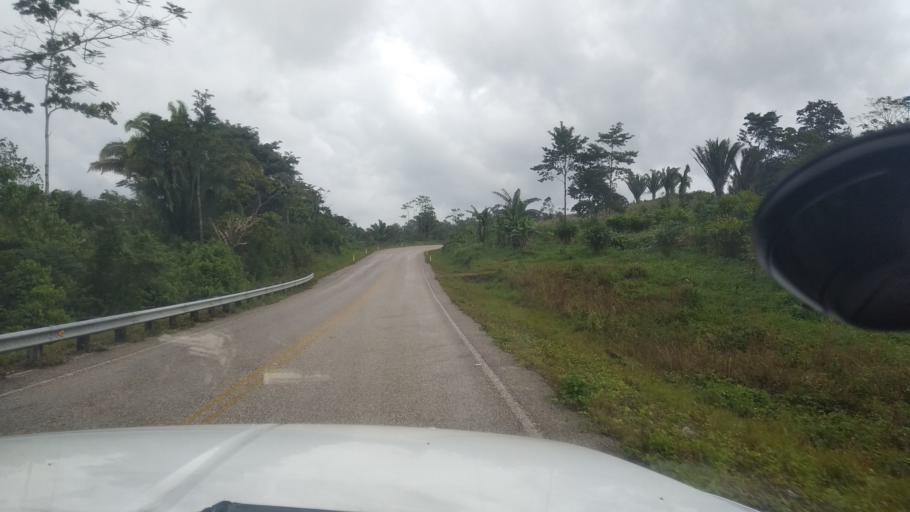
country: GT
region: Peten
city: San Luis
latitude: 16.1986
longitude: -89.1573
